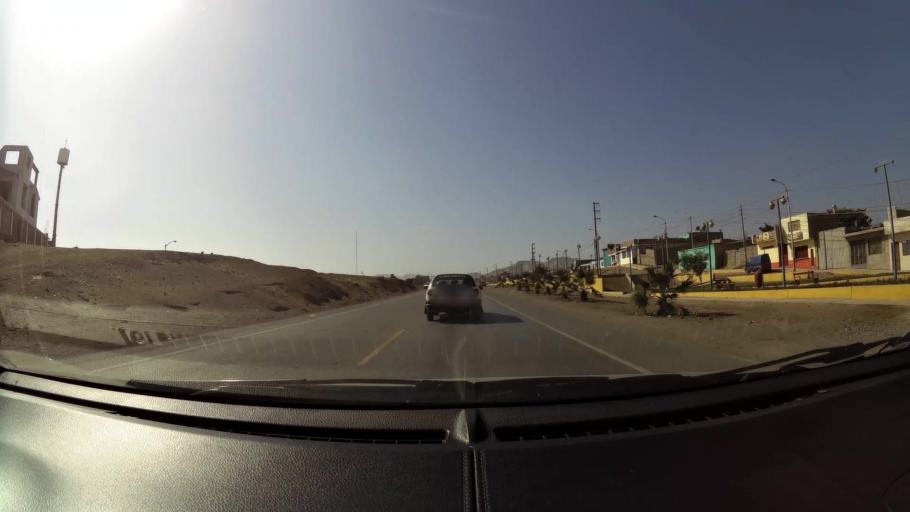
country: PE
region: Ancash
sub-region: Provincia de Huarmey
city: Huarmey
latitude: -10.0526
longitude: -78.1583
